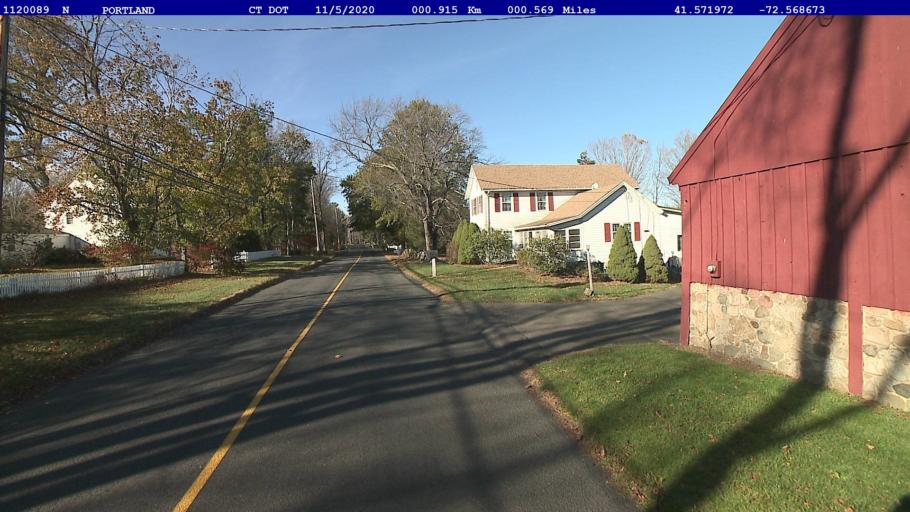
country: US
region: Connecticut
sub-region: Middlesex County
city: Lake Pocotopaug
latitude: 41.5720
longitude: -72.5687
